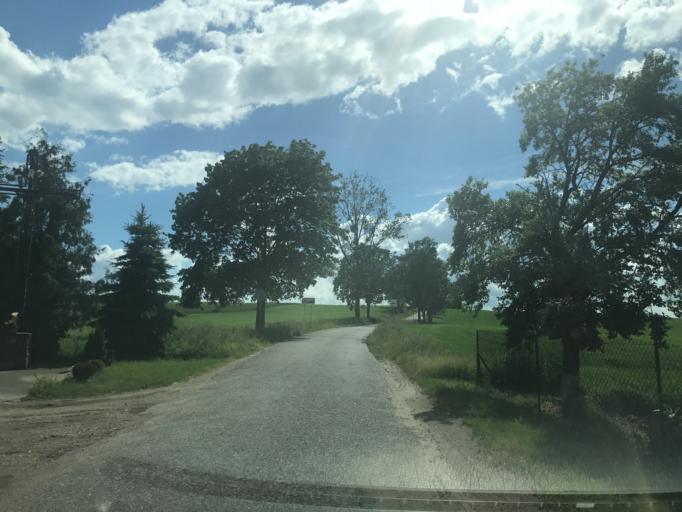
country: PL
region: Kujawsko-Pomorskie
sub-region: Powiat brodnicki
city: Brzozie
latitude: 53.3543
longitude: 19.6017
